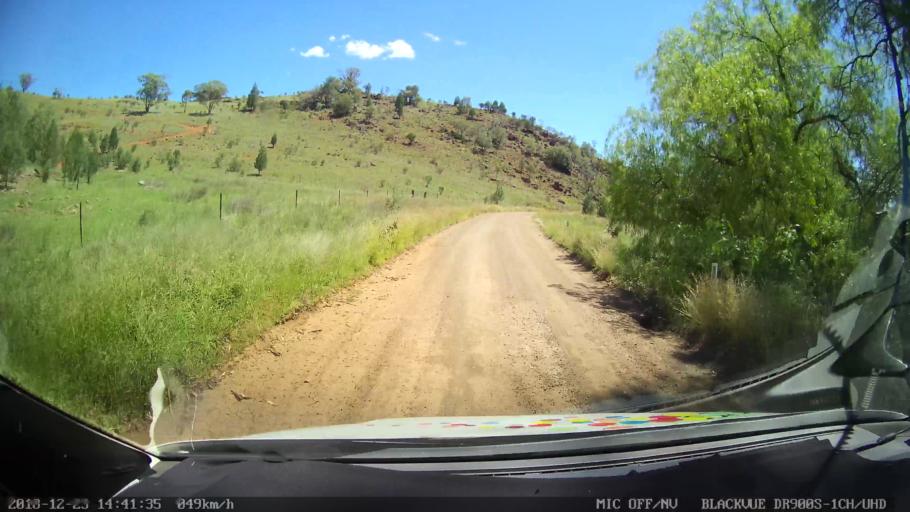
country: AU
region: New South Wales
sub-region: Tamworth Municipality
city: Manilla
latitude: -30.6325
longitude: 150.9015
